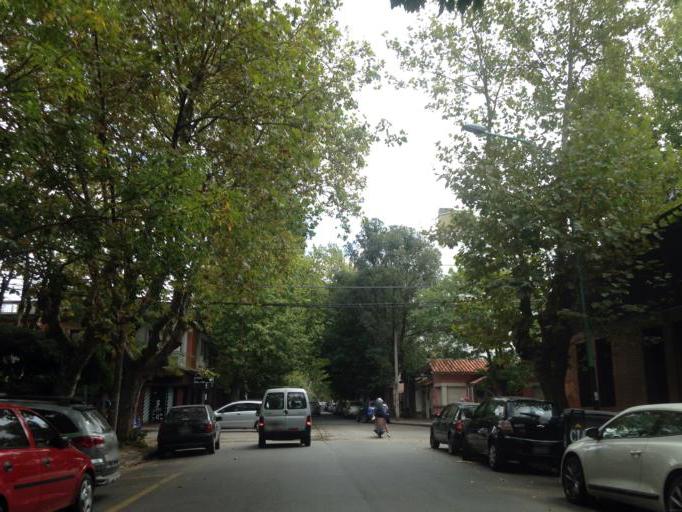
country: AR
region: Buenos Aires
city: Mar del Plata
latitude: -38.0057
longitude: -57.5570
